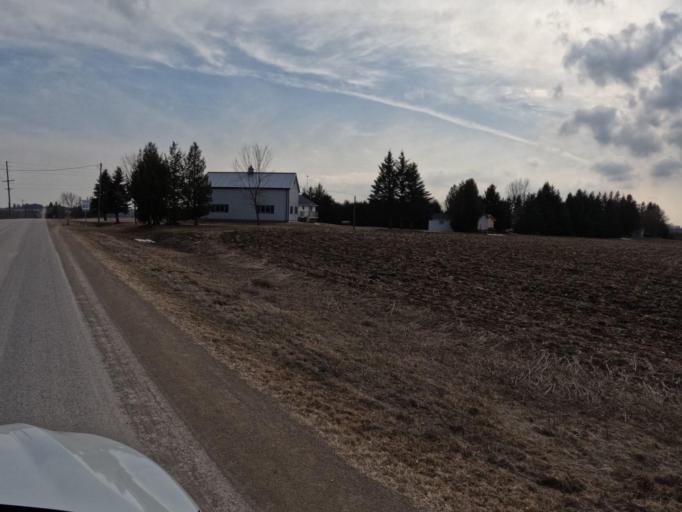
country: CA
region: Ontario
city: Shelburne
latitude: 43.9031
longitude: -80.3020
